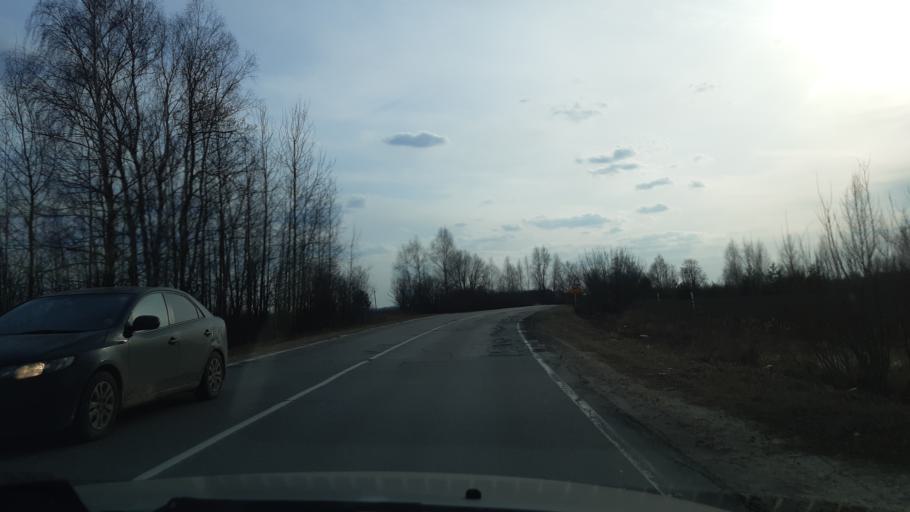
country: RU
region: Vladimir
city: Luknovo
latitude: 56.1910
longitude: 42.0267
